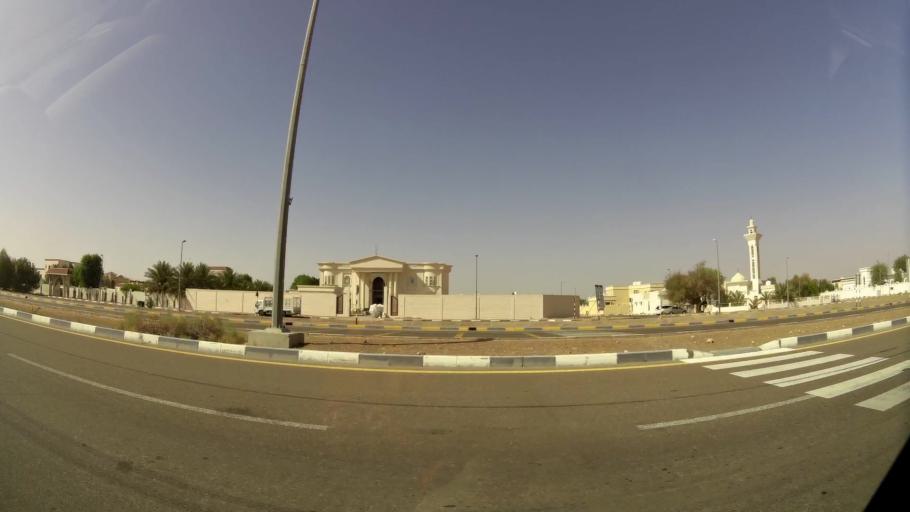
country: OM
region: Al Buraimi
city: Al Buraymi
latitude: 24.3412
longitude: 55.7997
